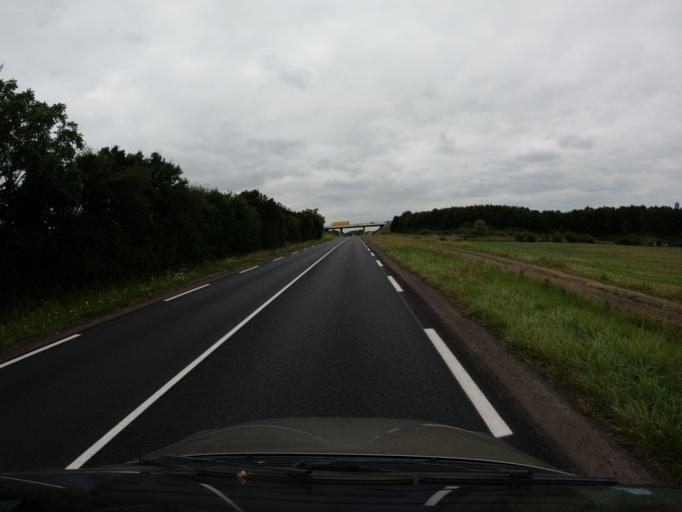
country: FR
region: Pays de la Loire
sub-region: Departement de la Vendee
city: Benet
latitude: 46.3928
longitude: -0.6422
